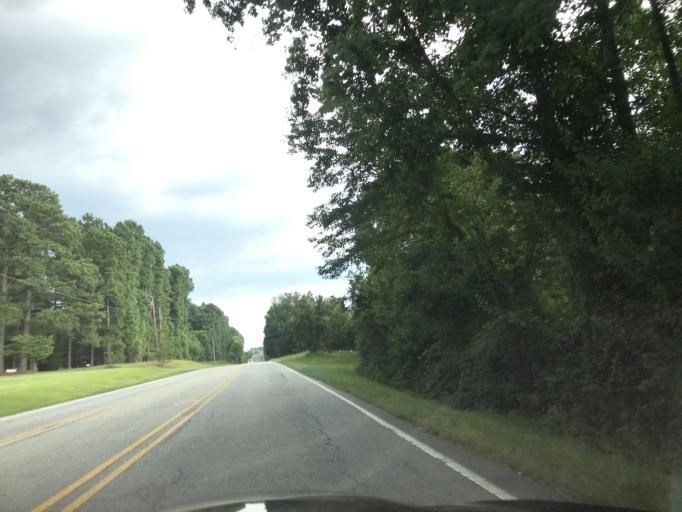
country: US
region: North Carolina
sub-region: Johnston County
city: Four Oaks
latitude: 35.5151
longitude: -78.4952
